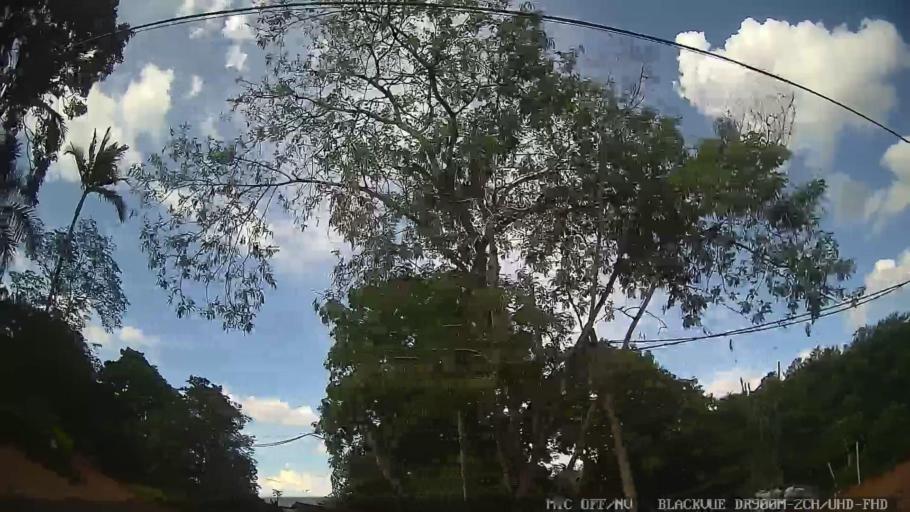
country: BR
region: Sao Paulo
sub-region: Jaguariuna
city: Jaguariuna
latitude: -22.6330
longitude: -47.0651
